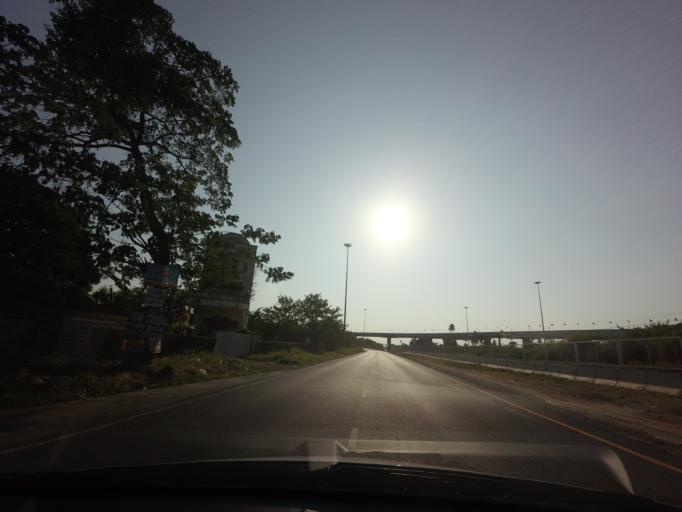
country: TH
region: Bangkok
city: Taling Chan
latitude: 13.7994
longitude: 100.4093
